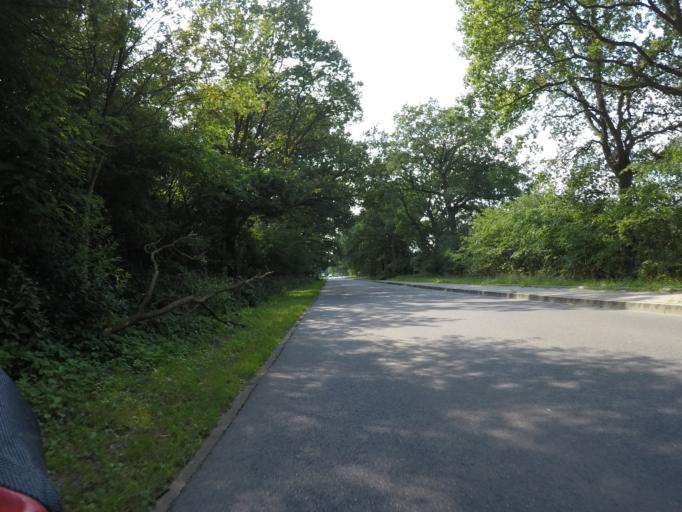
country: DE
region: Schleswig-Holstein
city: Tangstedt
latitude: 53.7114
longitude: 10.0587
